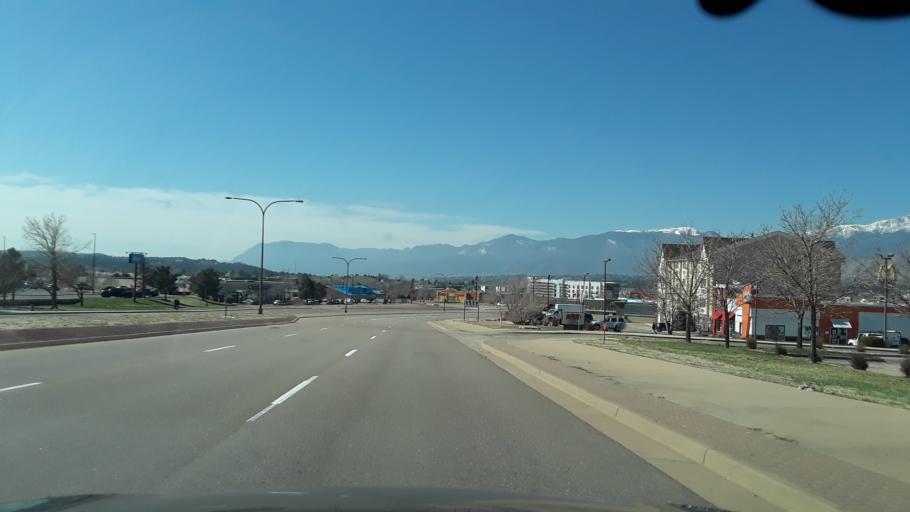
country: US
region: Colorado
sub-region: El Paso County
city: Air Force Academy
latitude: 38.9509
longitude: -104.8016
